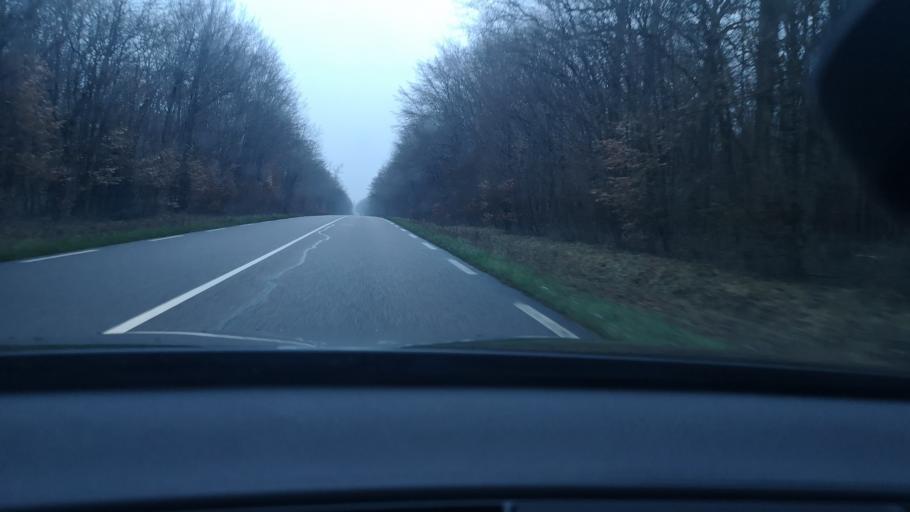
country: FR
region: Bourgogne
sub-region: Departement de la Cote-d'Or
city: Aiserey
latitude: 47.1057
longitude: 5.1022
